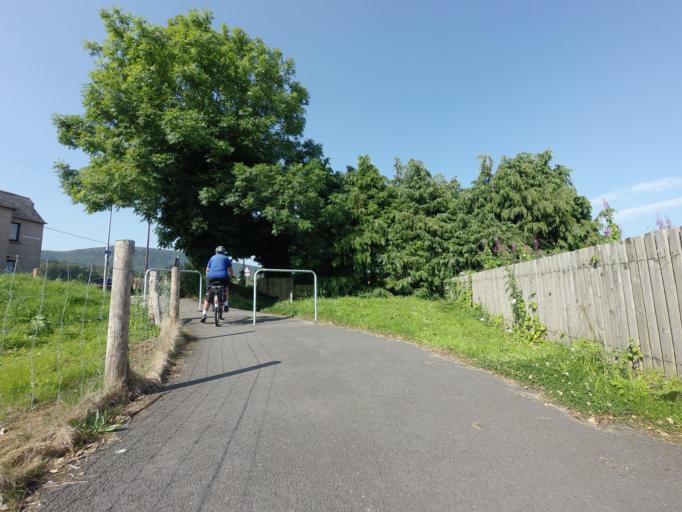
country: GB
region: Scotland
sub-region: Highland
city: Evanton
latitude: 57.6686
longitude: -4.3254
